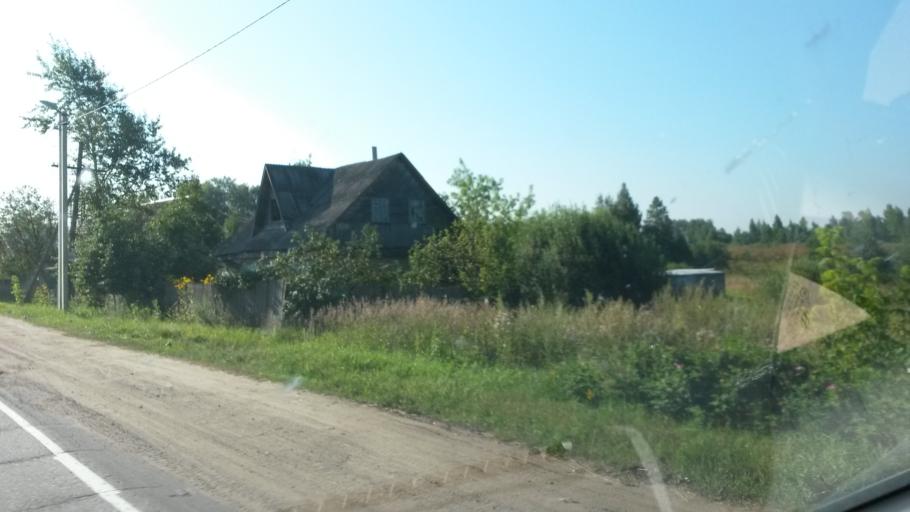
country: RU
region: Ivanovo
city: Novo-Talitsy
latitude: 57.0672
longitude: 40.6992
